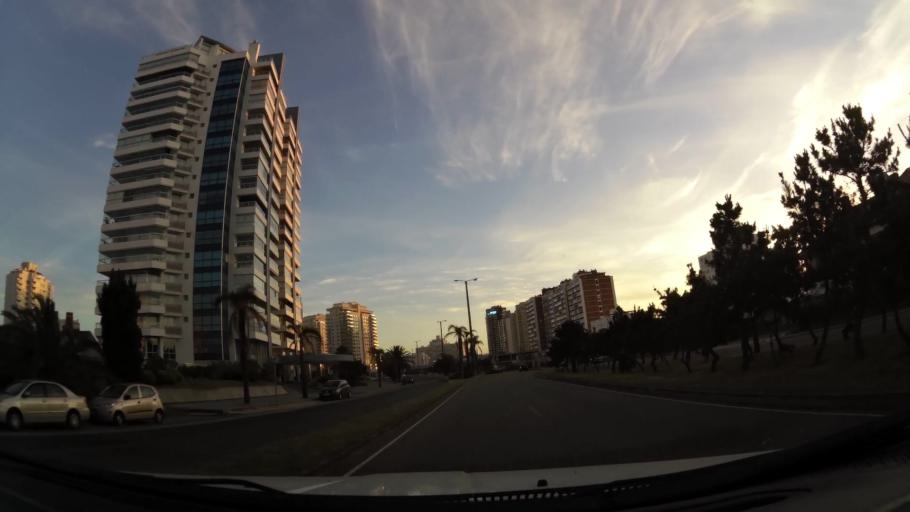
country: UY
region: Maldonado
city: Punta del Este
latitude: -34.9528
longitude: -54.9383
